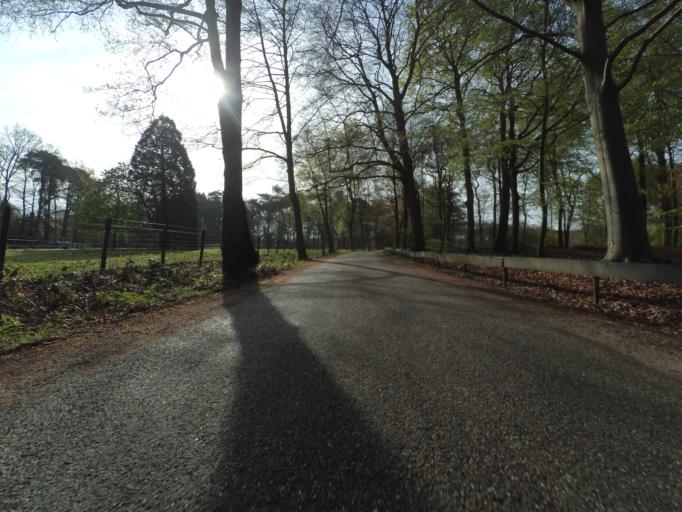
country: NL
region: Utrecht
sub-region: Gemeente Utrechtse Heuvelrug
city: Doorn
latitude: 52.0304
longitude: 5.3578
